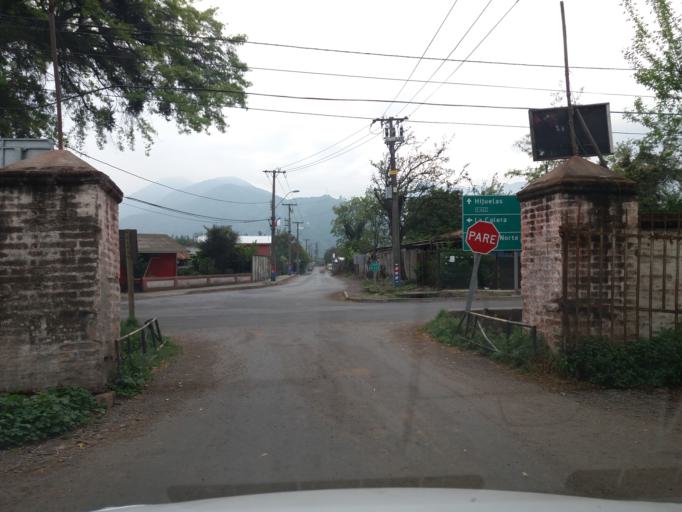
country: CL
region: Valparaiso
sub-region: Provincia de Quillota
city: Hacienda La Calera
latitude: -32.8493
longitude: -71.1037
